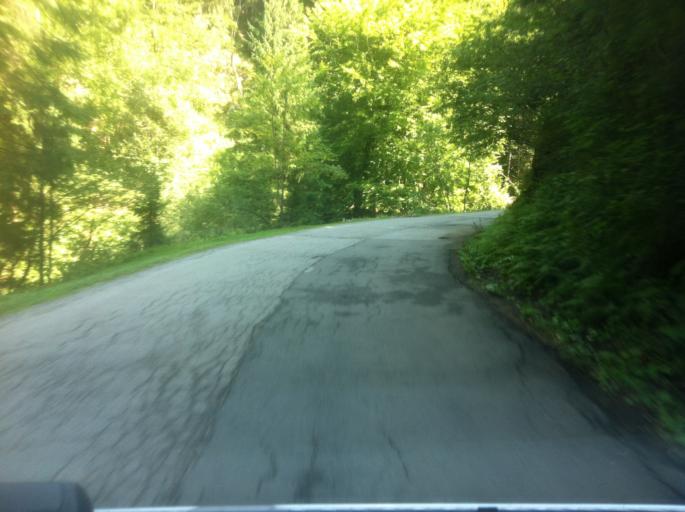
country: RO
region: Hunedoara
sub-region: Oras Petrila
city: Petrila
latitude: 45.4091
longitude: 23.4889
